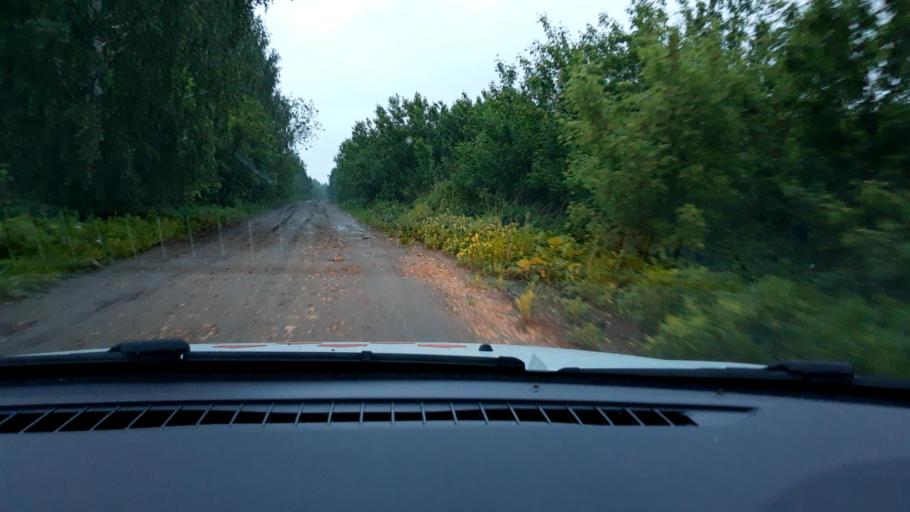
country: RU
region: Nizjnij Novgorod
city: Novaya Balakhna
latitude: 56.6328
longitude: 43.6269
